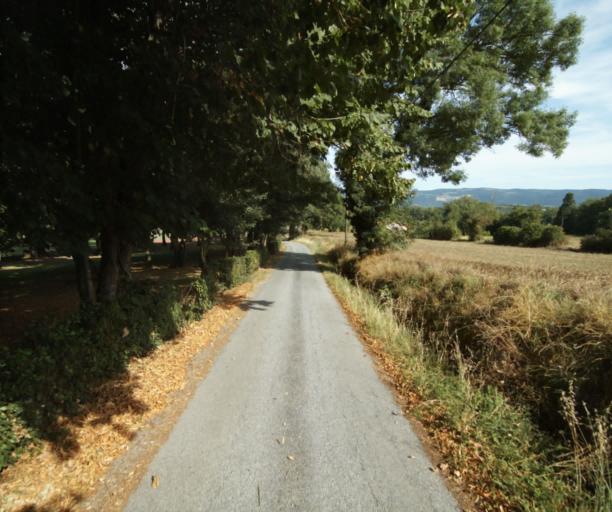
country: FR
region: Midi-Pyrenees
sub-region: Departement du Tarn
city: Soual
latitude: 43.5328
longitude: 2.0770
